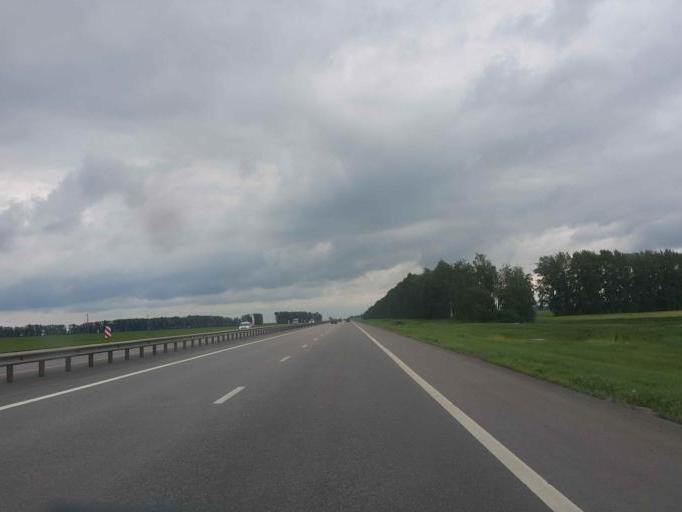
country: RU
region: Tambov
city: Zavoronezhskoye
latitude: 52.8358
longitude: 40.8652
